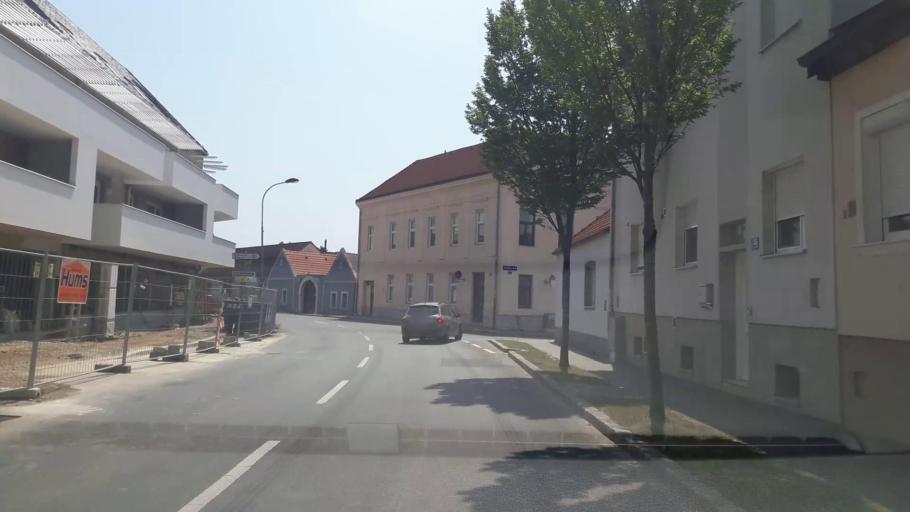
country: AT
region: Lower Austria
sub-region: Politischer Bezirk Bruck an der Leitha
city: Bruck an der Leitha
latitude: 48.0124
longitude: 16.7219
